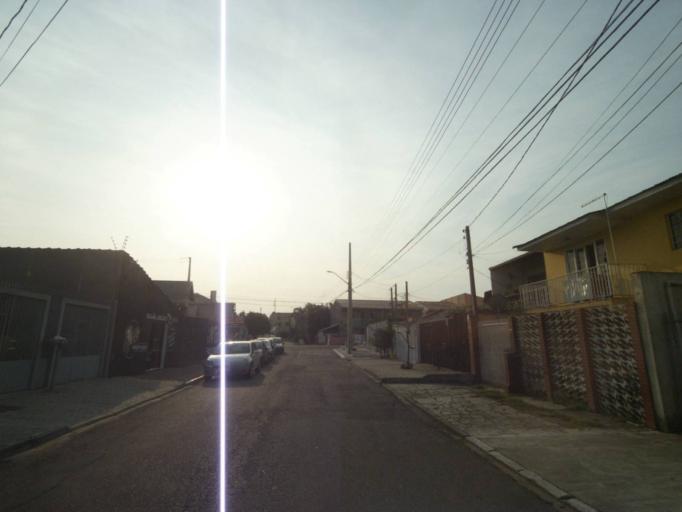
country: BR
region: Parana
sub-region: Pinhais
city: Pinhais
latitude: -25.4804
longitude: -49.2009
